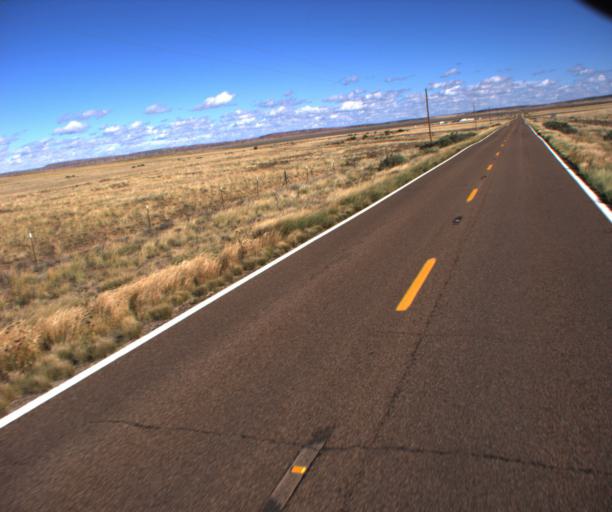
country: US
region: Arizona
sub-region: Apache County
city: Saint Johns
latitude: 34.5861
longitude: -109.3308
